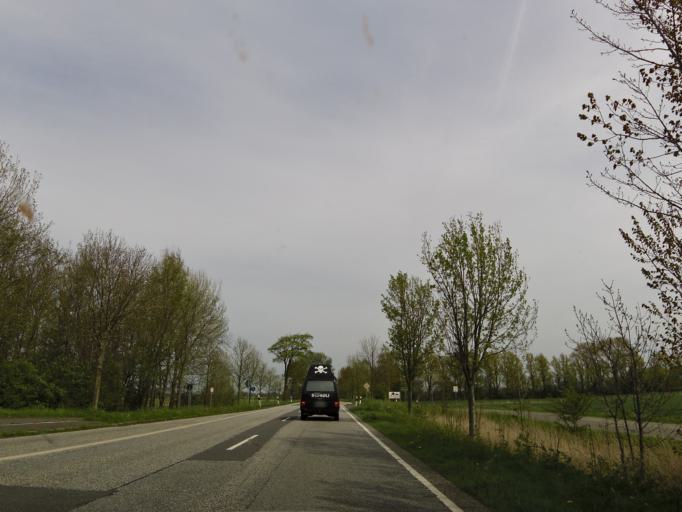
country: DE
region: Schleswig-Holstein
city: Tonning
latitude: 54.3368
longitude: 8.9604
